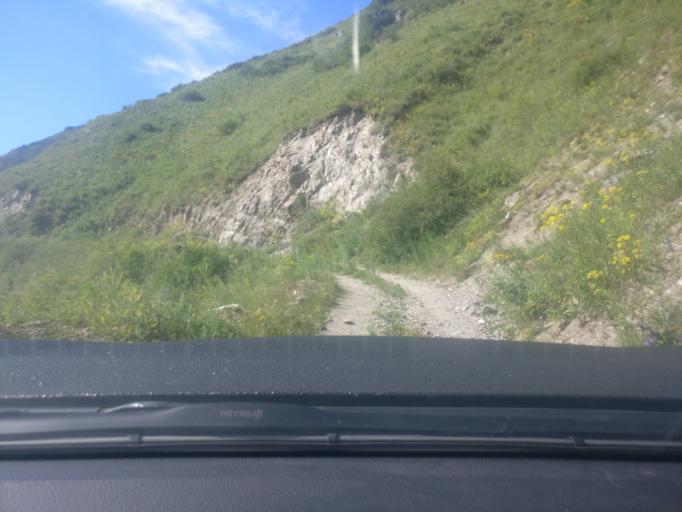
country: KZ
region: Almaty Qalasy
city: Almaty
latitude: 43.1006
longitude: 76.9523
